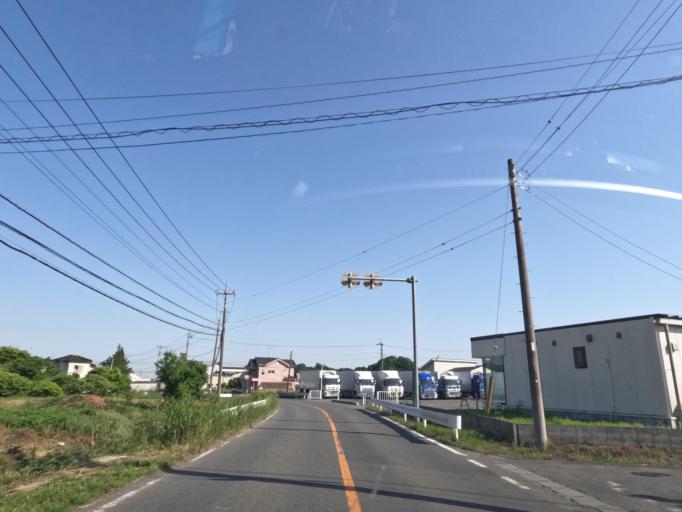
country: JP
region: Saitama
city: Ogawa
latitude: 36.0699
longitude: 139.2978
